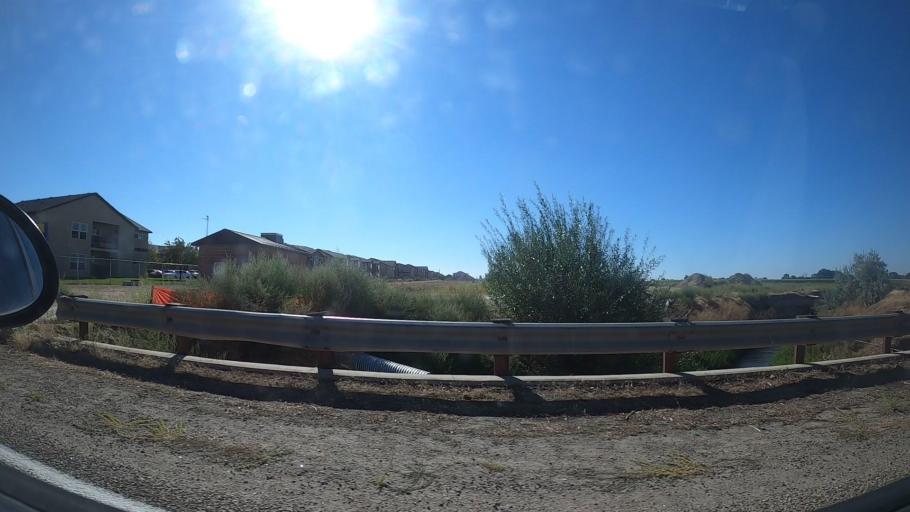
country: US
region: Idaho
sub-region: Canyon County
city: Nampa
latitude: 43.6023
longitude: -116.6133
